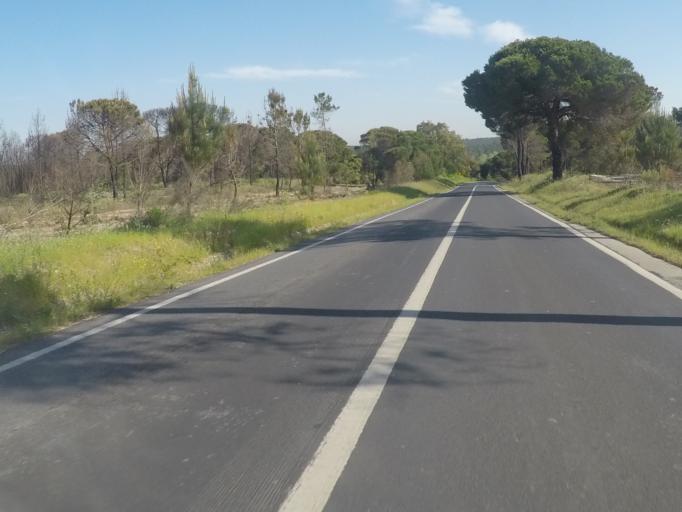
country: PT
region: Setubal
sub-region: Sesimbra
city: Sesimbra
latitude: 38.5204
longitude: -9.1435
